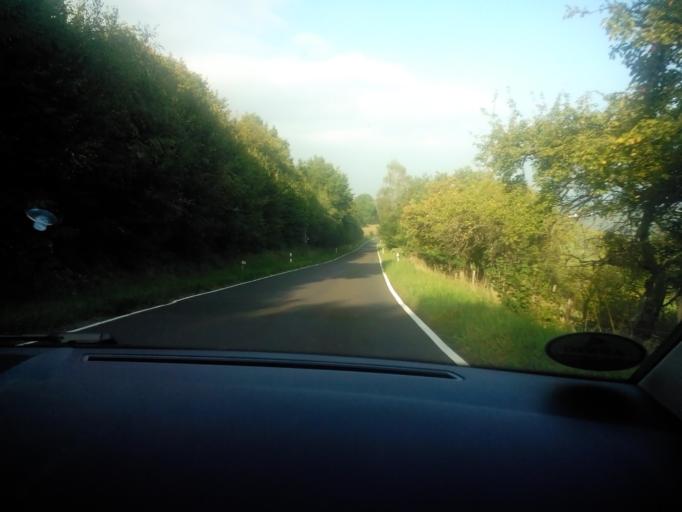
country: DE
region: Rheinland-Pfalz
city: Irsch
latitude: 49.5746
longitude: 6.6097
